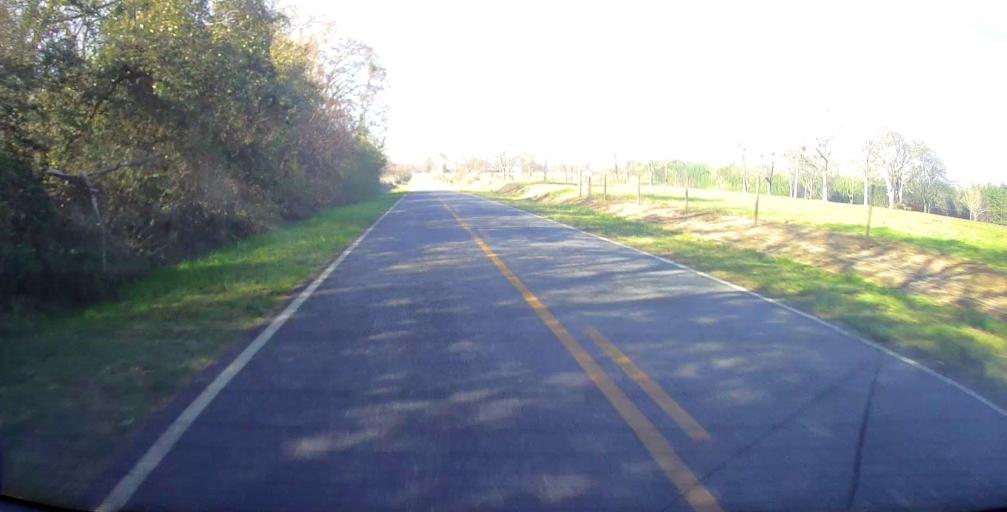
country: US
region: Georgia
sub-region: Peach County
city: Fort Valley
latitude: 32.6107
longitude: -83.8522
